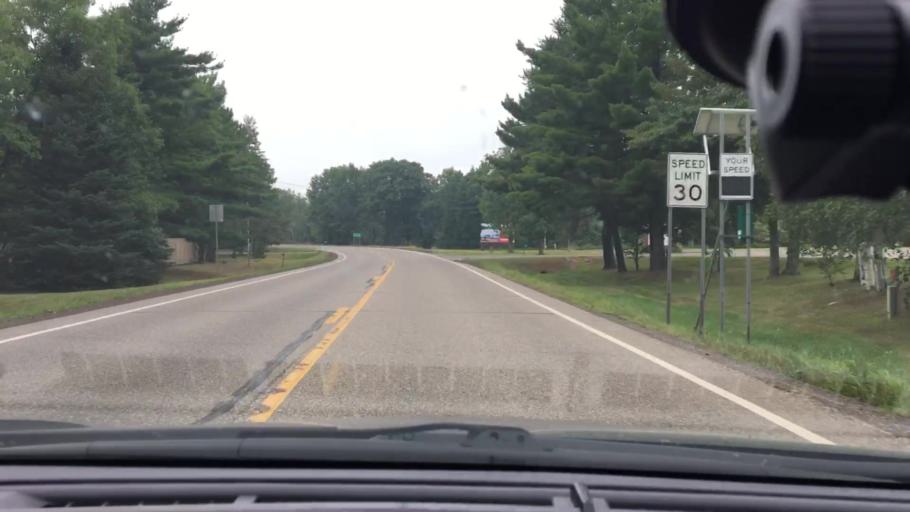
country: US
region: Minnesota
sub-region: Crow Wing County
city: Cross Lake
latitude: 46.8261
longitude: -93.9473
